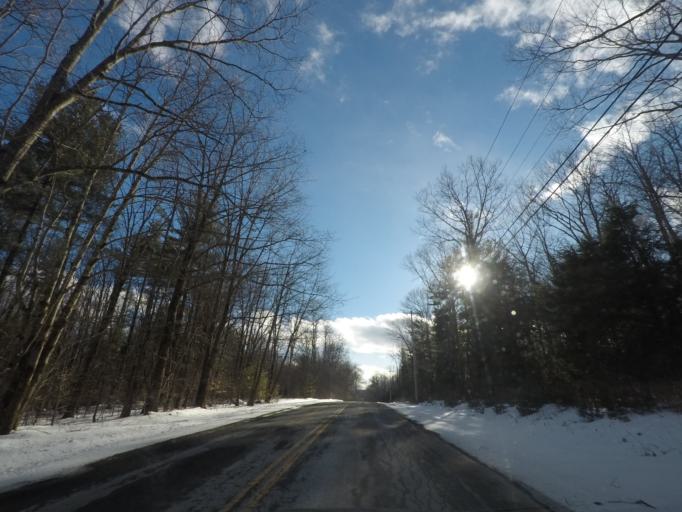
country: US
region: New York
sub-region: Rensselaer County
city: Hoosick Falls
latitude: 42.8076
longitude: -73.3951
